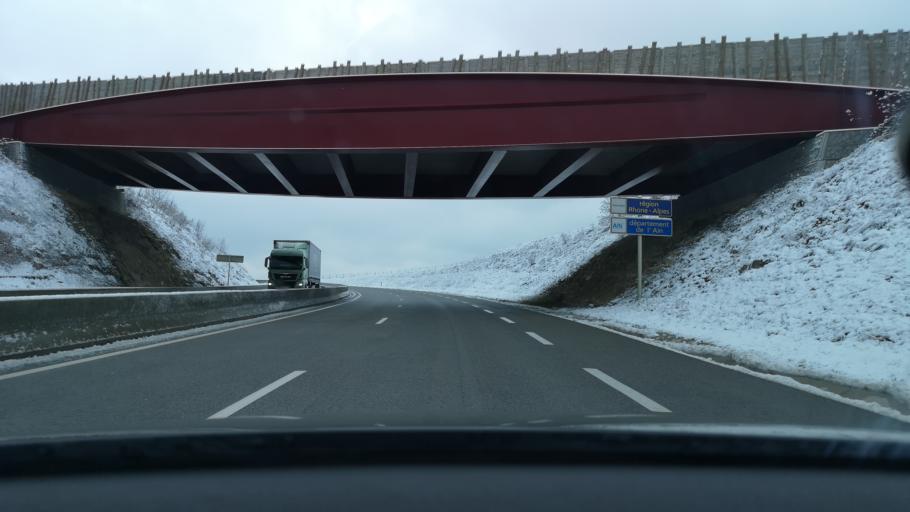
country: FR
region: Rhone-Alpes
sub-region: Departement de l'Ain
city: Dortan
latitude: 46.3191
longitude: 5.6725
